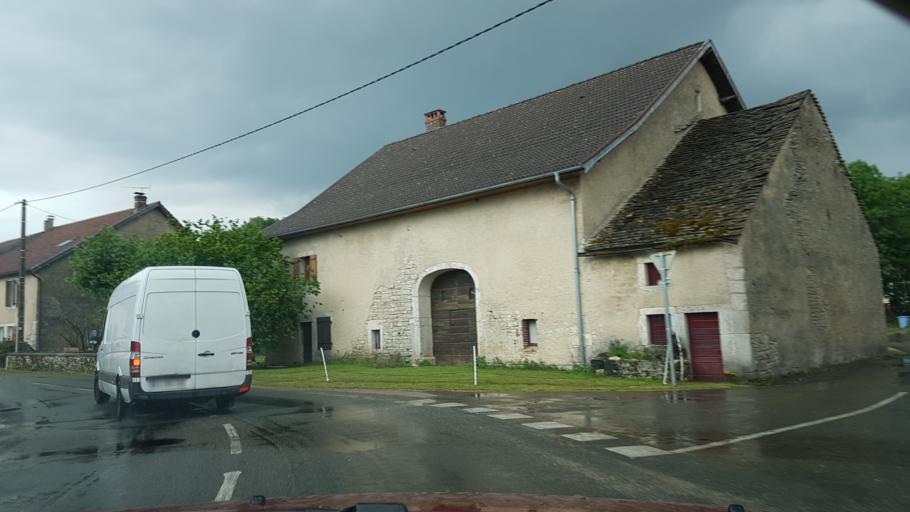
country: FR
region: Franche-Comte
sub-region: Departement du Jura
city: Clairvaux-les-Lacs
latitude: 46.5334
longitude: 5.7370
